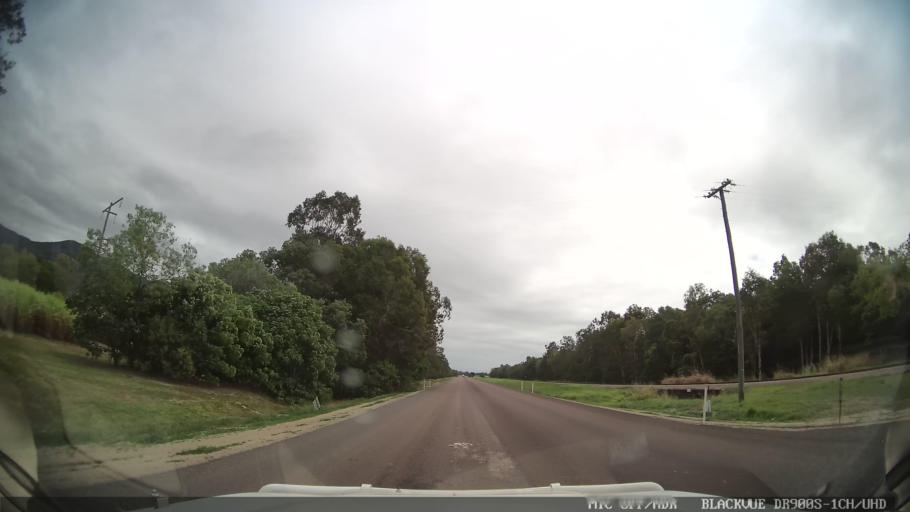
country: AU
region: Queensland
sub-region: Hinchinbrook
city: Ingham
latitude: -18.9295
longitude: 146.2658
